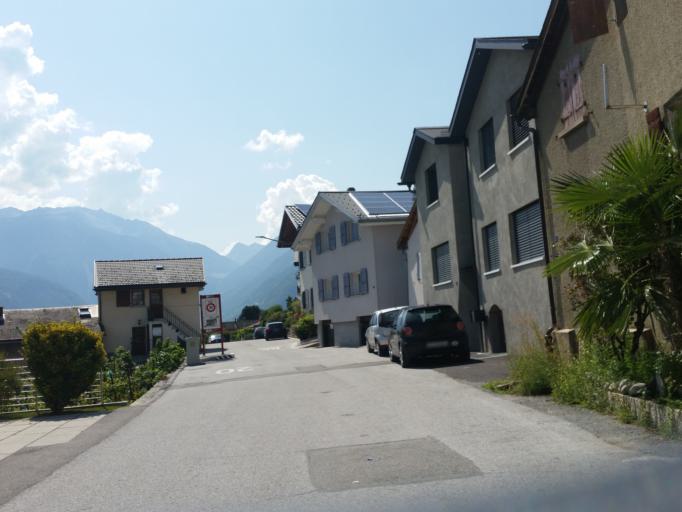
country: CH
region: Valais
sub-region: Martigny District
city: Fully
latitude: 46.1343
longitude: 7.1074
